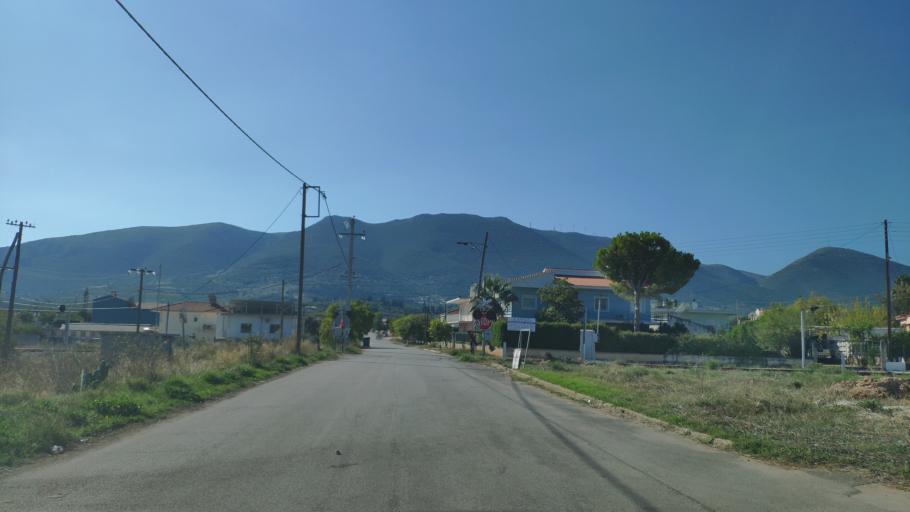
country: GR
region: Peloponnese
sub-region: Nomos Korinthias
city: Khiliomodhi
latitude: 37.8051
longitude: 22.8701
